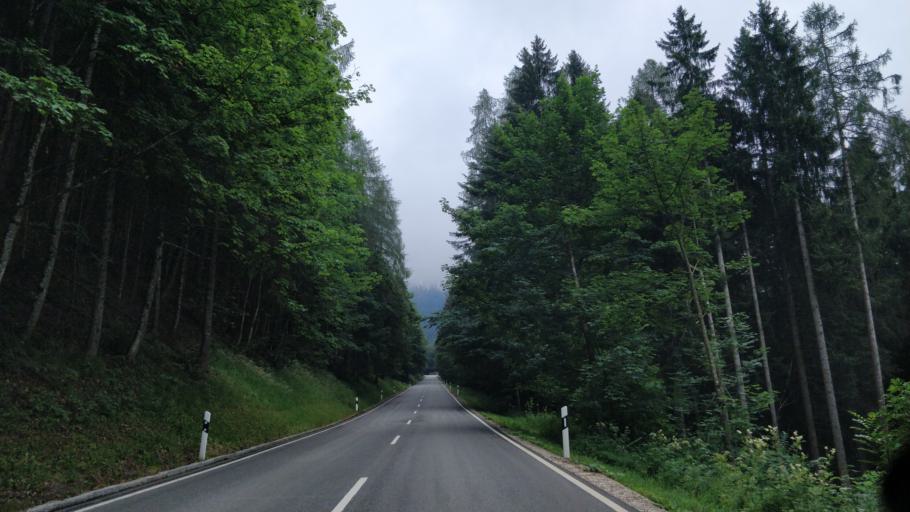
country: AT
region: Salzburg
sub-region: Politischer Bezirk Hallein
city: Hallein
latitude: 47.6491
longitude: 13.0796
